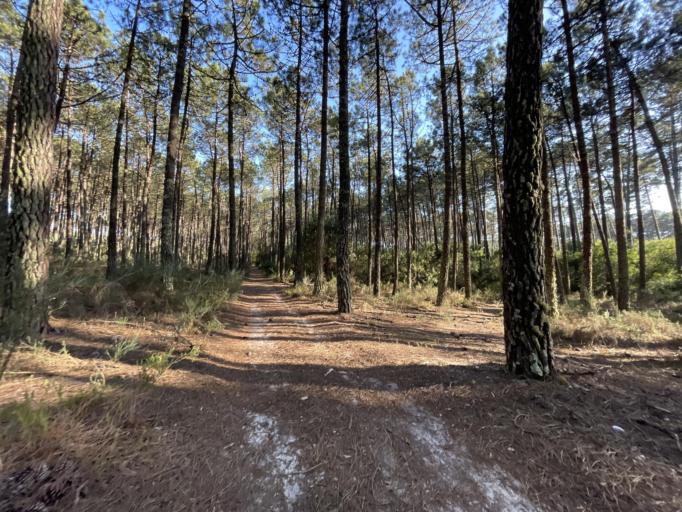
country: PT
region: Aveiro
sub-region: Ovar
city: Cortegaca
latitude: 40.9362
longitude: -8.6413
